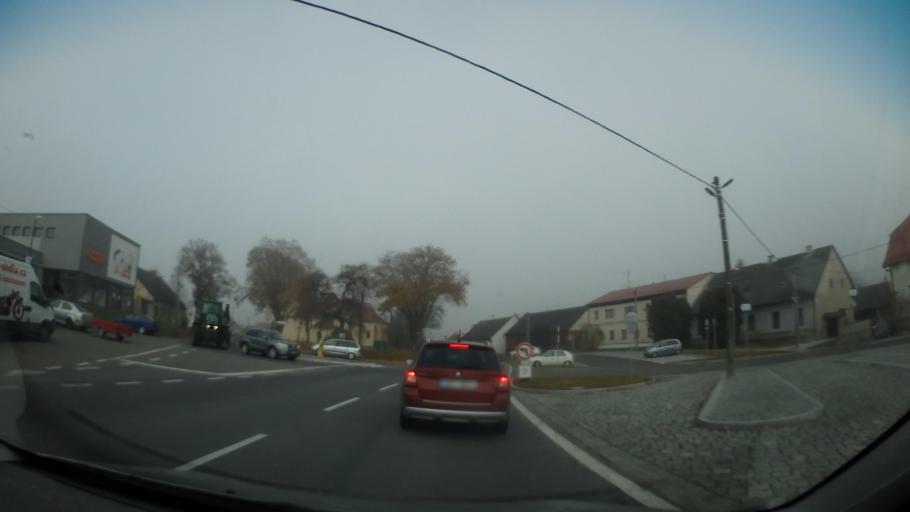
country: CZ
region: Vysocina
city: Krizanov
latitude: 49.4752
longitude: 16.1191
